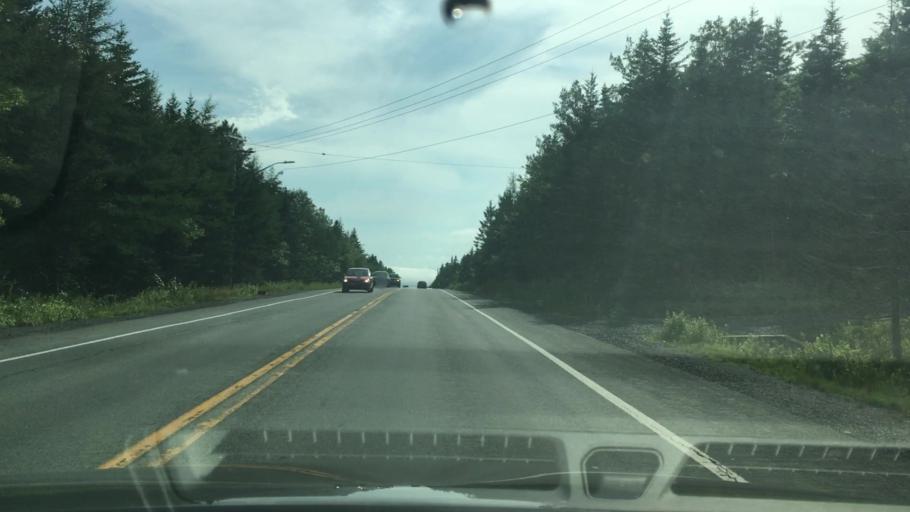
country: CA
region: Nova Scotia
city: Dartmouth
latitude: 44.7154
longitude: -63.8316
